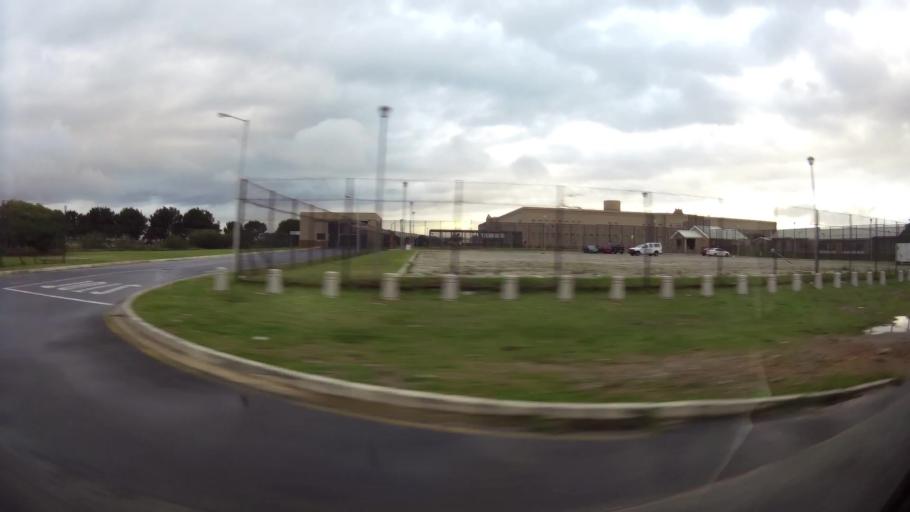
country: ZA
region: Eastern Cape
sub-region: Nelson Mandela Bay Metropolitan Municipality
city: Port Elizabeth
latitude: -33.9272
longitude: 25.6074
